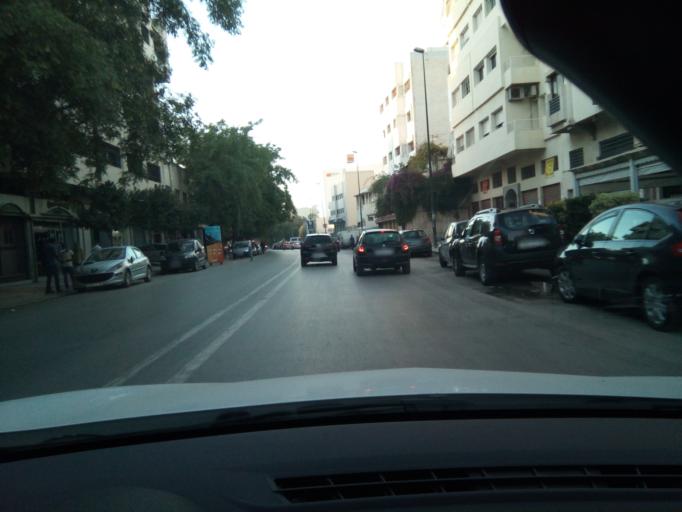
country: MA
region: Fes-Boulemane
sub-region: Fes
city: Fes
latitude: 34.0309
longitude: -4.9935
